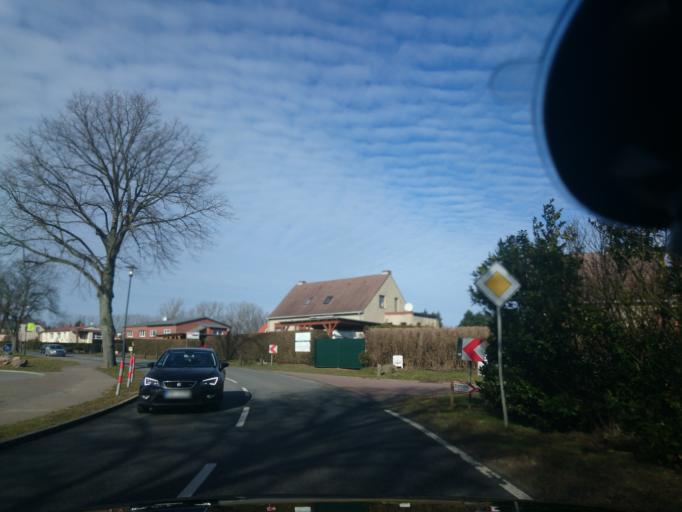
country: DE
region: Mecklenburg-Vorpommern
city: Elmenhorst
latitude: 54.1570
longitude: 12.0105
